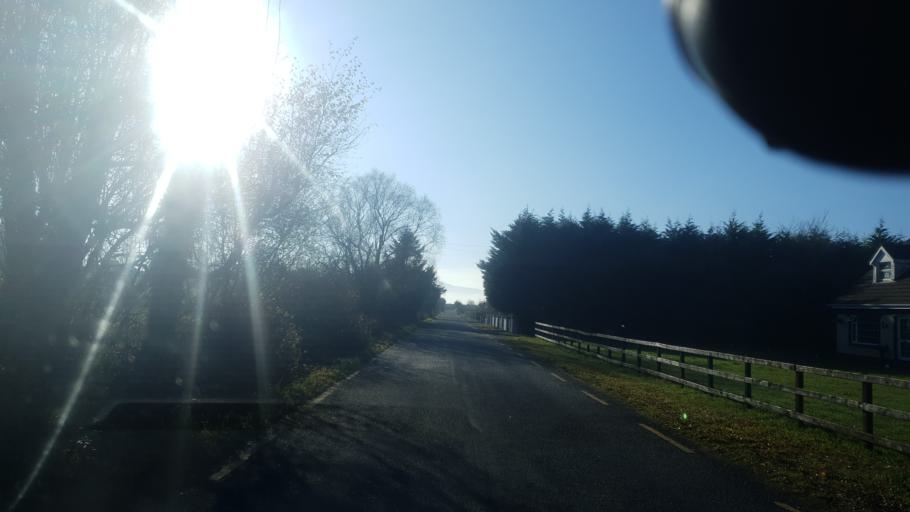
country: IE
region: Munster
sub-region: Ciarrai
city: Cill Airne
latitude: 52.1074
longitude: -9.4713
